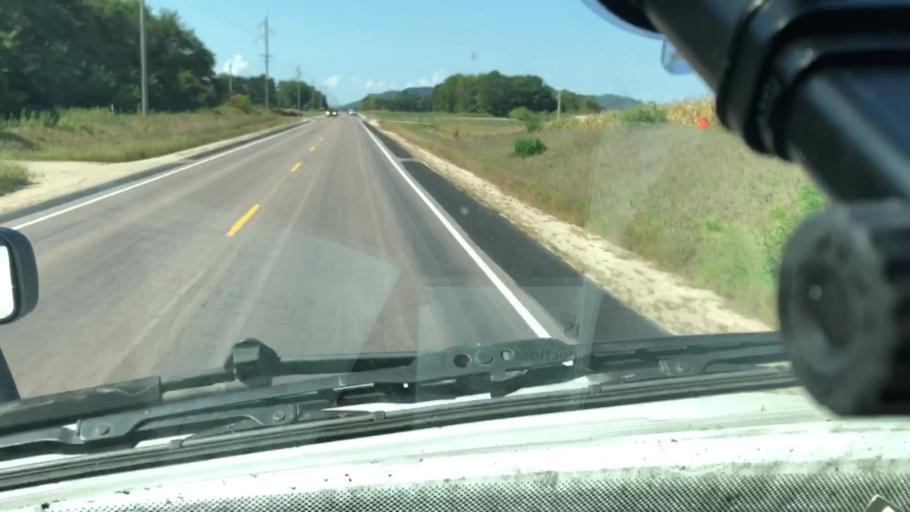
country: US
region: Wisconsin
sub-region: Trempealeau County
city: Trempealeau
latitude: 44.0701
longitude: -91.5039
